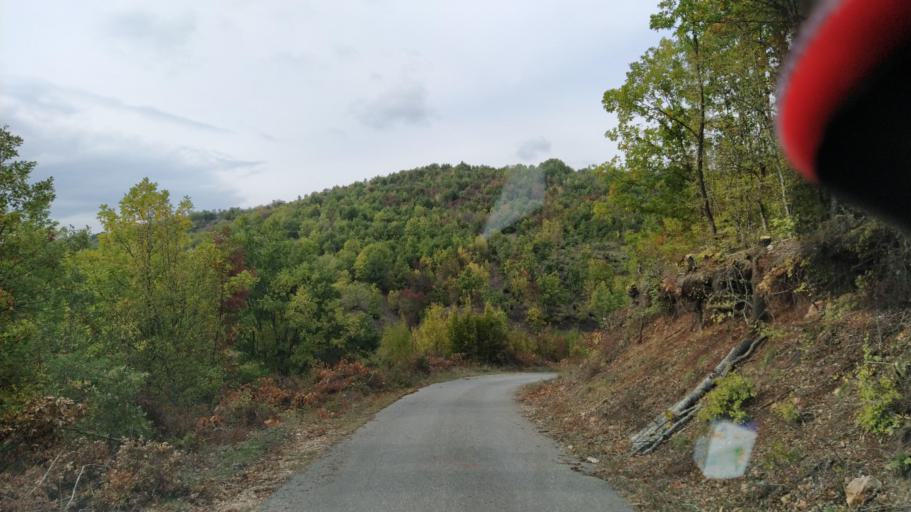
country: MK
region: Strumica
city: Veljusa
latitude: 41.5109
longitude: 22.4860
